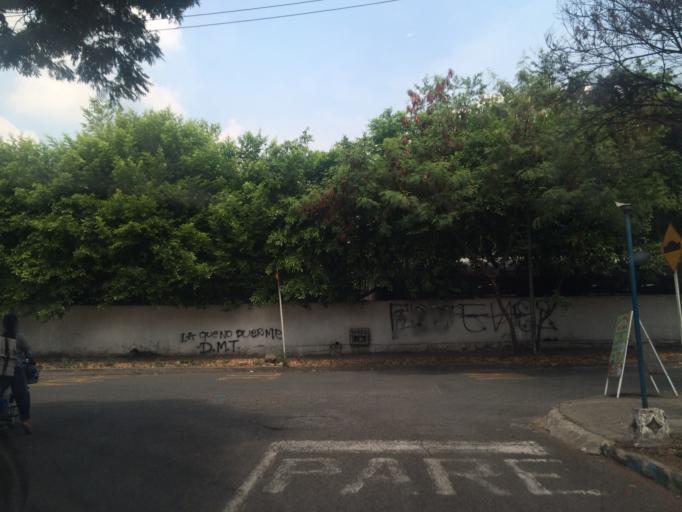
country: CO
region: Valle del Cauca
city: Cali
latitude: 3.4937
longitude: -76.4895
